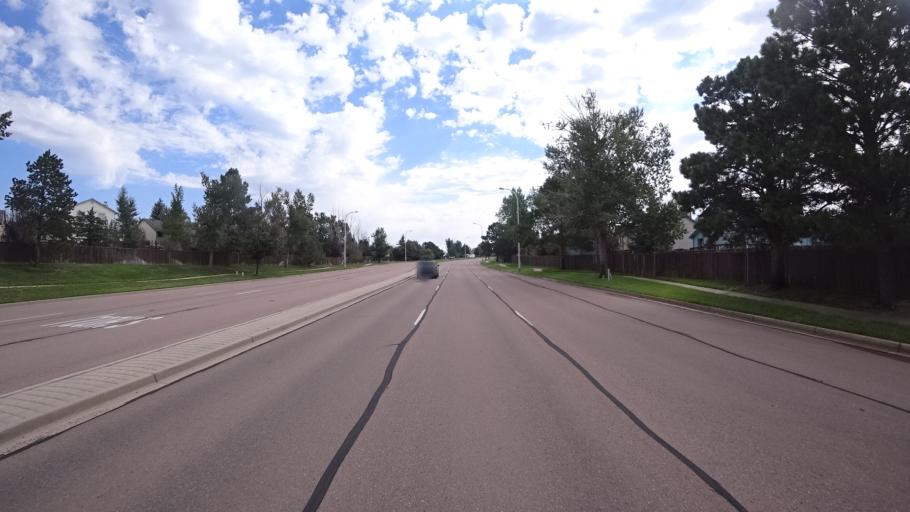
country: US
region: Colorado
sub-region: El Paso County
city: Cimarron Hills
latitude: 38.9016
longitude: -104.7006
